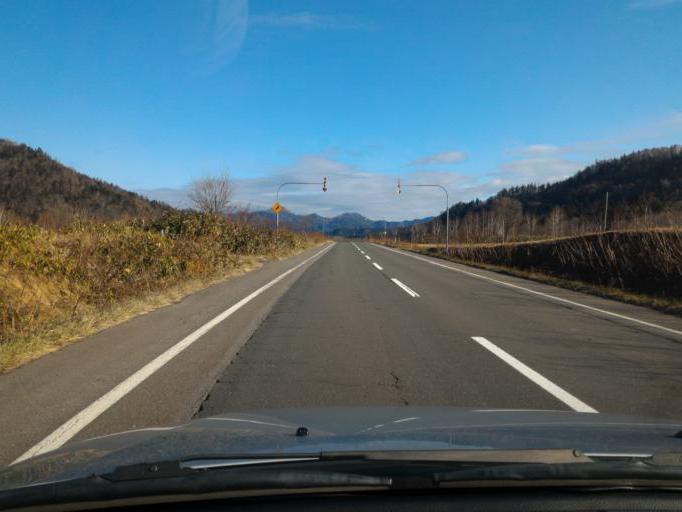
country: JP
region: Hokkaido
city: Ashibetsu
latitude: 43.3044
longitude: 142.1164
